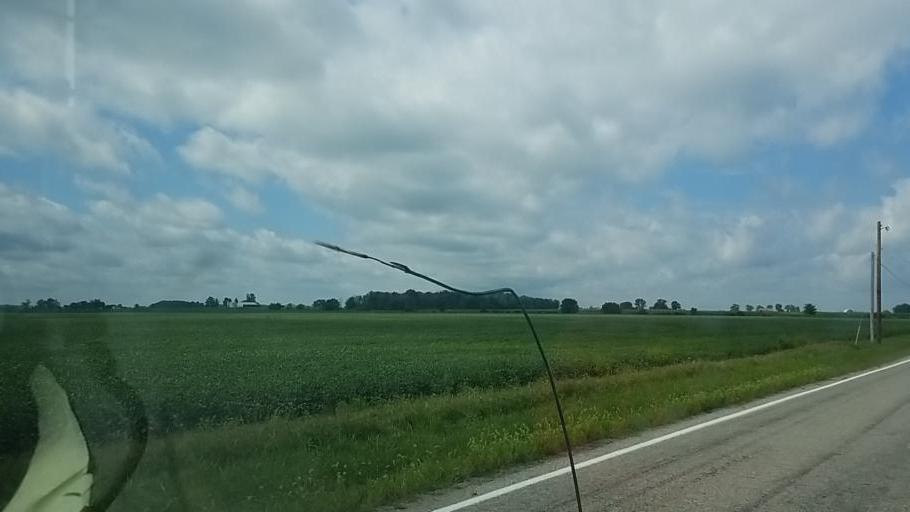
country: US
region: Ohio
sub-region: Madison County
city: Bethel
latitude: 39.7315
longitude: -83.4061
